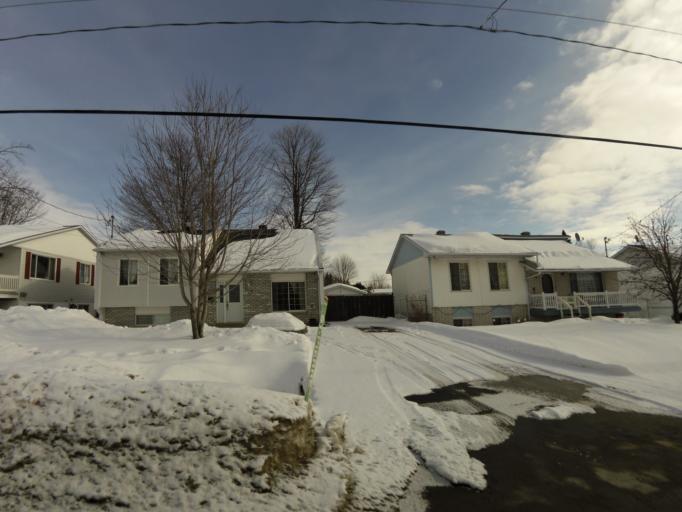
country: CA
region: Quebec
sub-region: Outaouais
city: Gatineau
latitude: 45.5013
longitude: -75.5812
